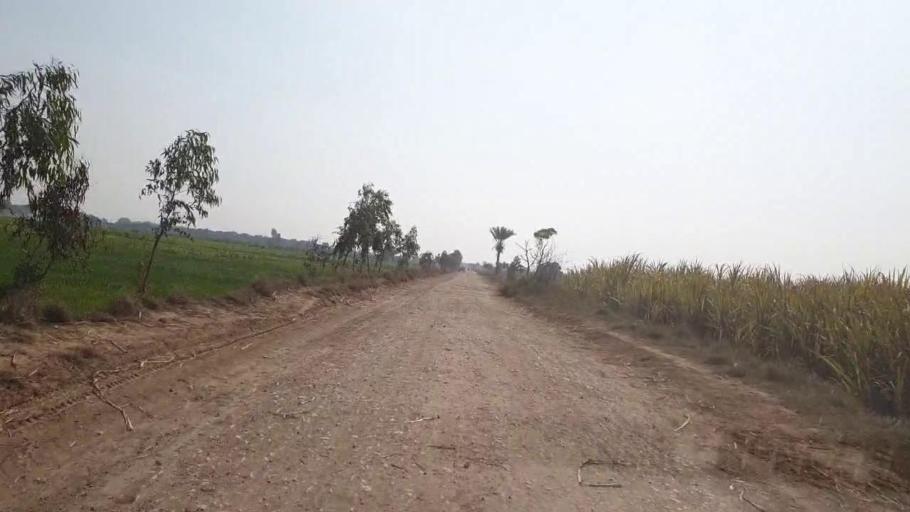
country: PK
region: Sindh
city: Bhit Shah
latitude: 25.7157
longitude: 68.5458
